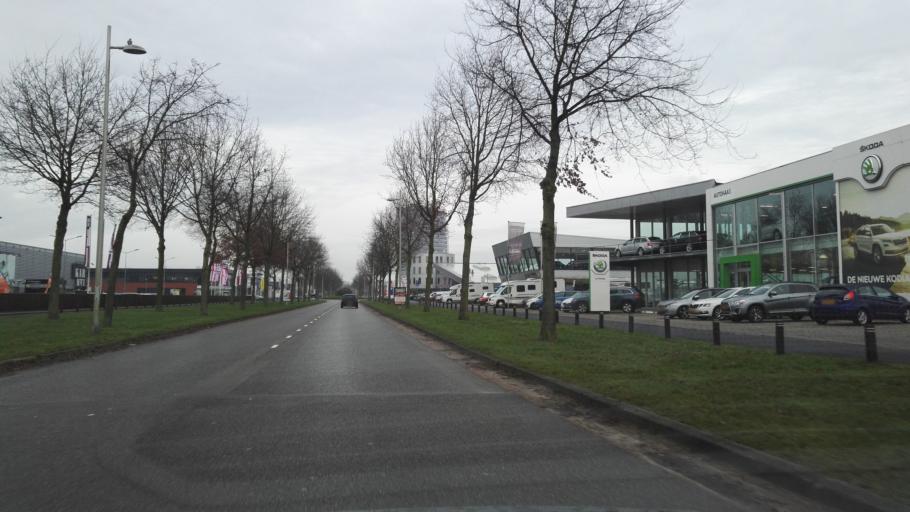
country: NL
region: Gelderland
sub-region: Gemeente Apeldoorn
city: Apeldoorn
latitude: 52.2369
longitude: 5.9882
